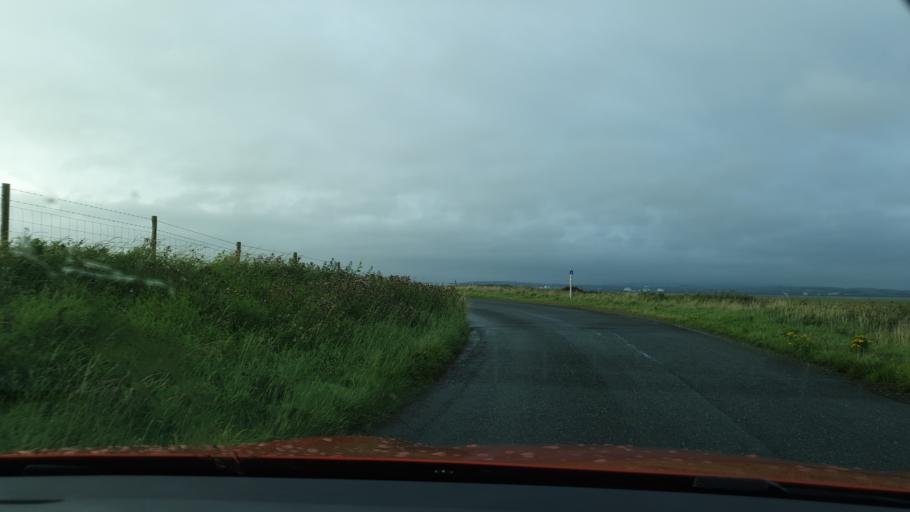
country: GB
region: England
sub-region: Cumbria
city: Barrow in Furness
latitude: 54.0679
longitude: -3.2253
